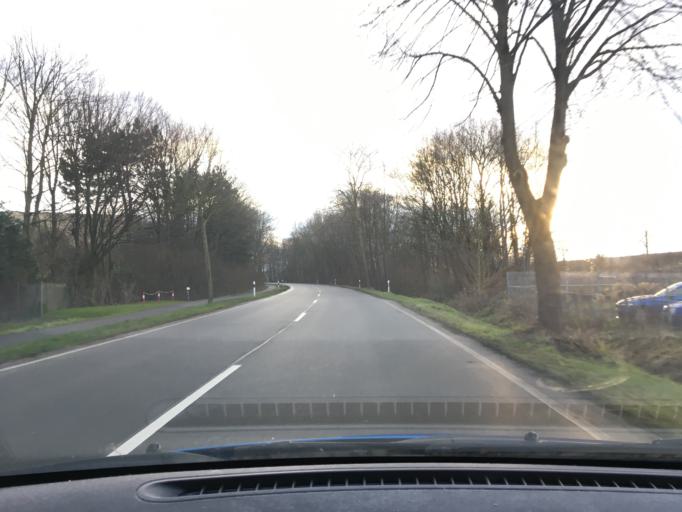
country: DE
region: Lower Saxony
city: Langenhagen
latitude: 52.4520
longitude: 9.7228
